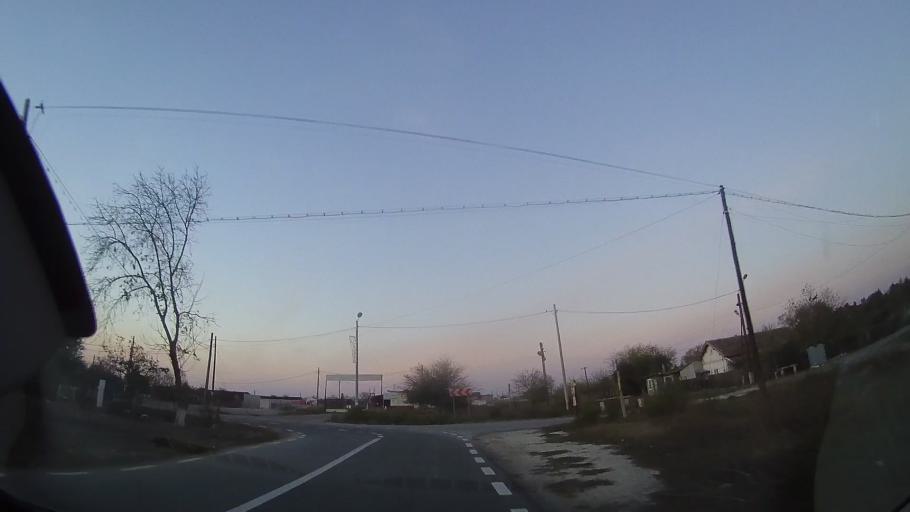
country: RO
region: Constanta
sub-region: Comuna Cobadin
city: Cobadin
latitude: 44.0550
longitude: 28.2462
